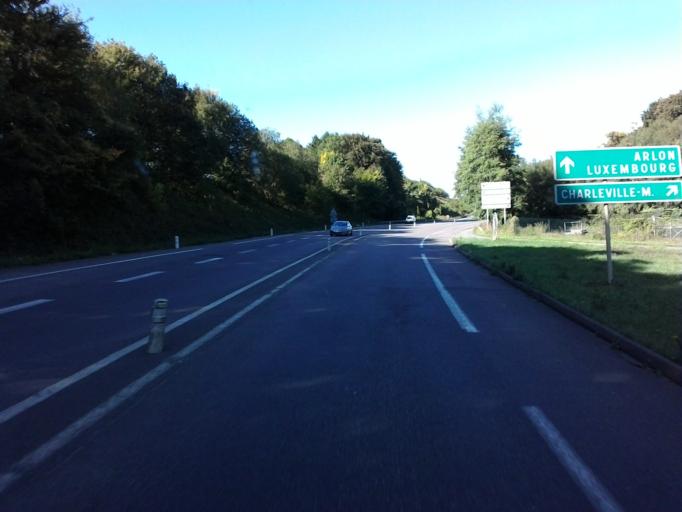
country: FR
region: Lorraine
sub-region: Departement de Meurthe-et-Moselle
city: Rehon
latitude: 49.5131
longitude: 5.7489
